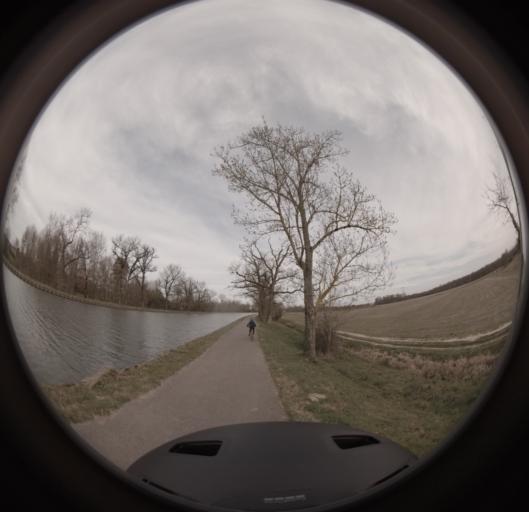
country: FR
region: Midi-Pyrenees
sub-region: Departement du Tarn-et-Garonne
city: Montech
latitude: 43.9823
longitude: 1.2549
